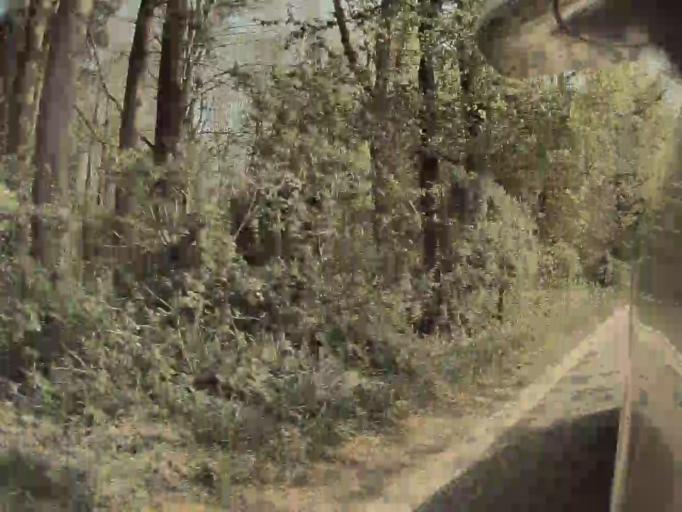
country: BE
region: Wallonia
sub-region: Province de Namur
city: Havelange
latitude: 50.3158
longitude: 5.2401
